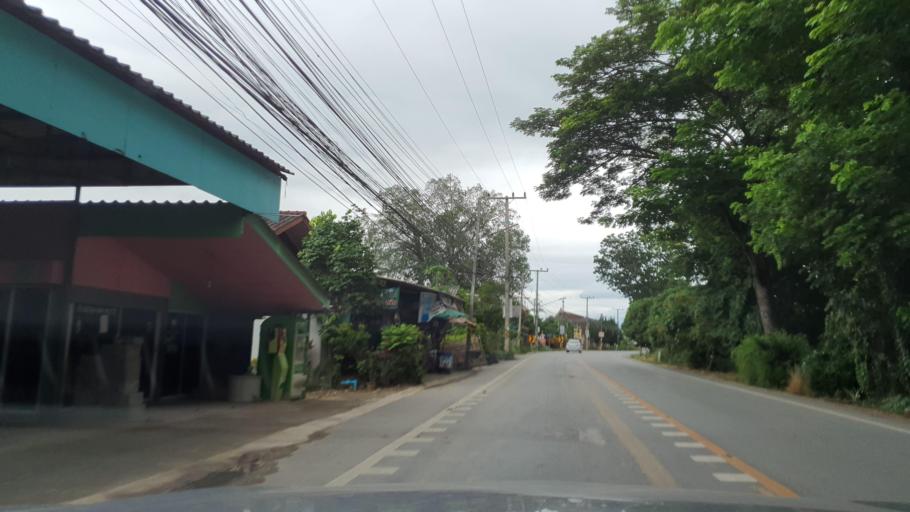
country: TH
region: Lamphun
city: Lamphun
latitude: 18.6139
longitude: 98.9564
